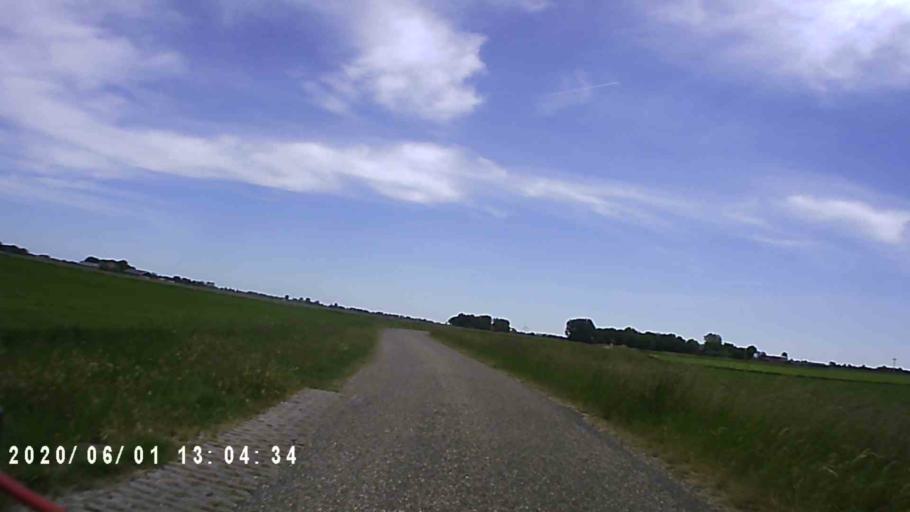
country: NL
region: Friesland
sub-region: Gemeente Franekeradeel
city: Tzum
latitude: 53.1423
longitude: 5.5381
